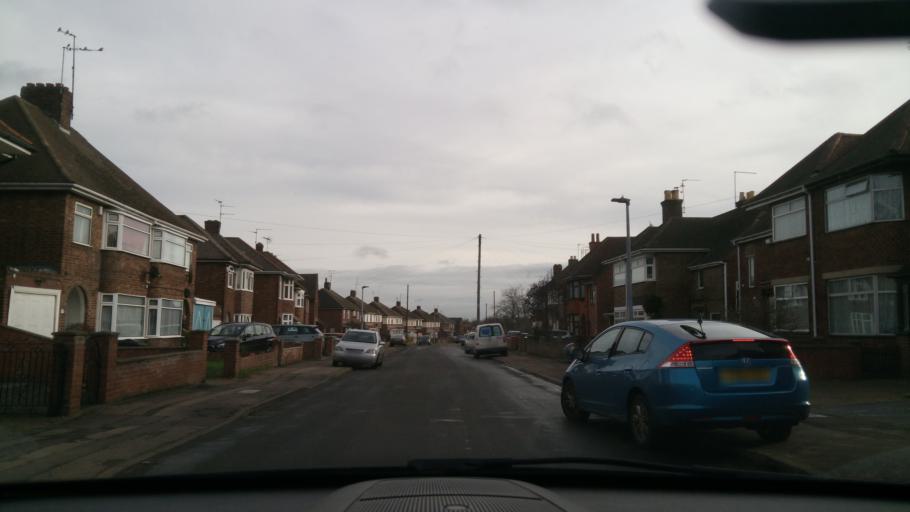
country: GB
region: England
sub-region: Peterborough
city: Peterborough
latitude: 52.5869
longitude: -0.2229
